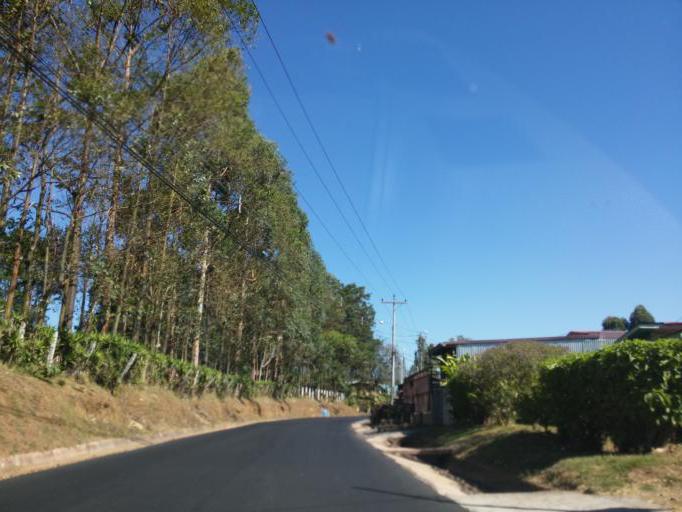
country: CR
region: Alajuela
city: Sabanilla
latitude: 10.0737
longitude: -84.1939
